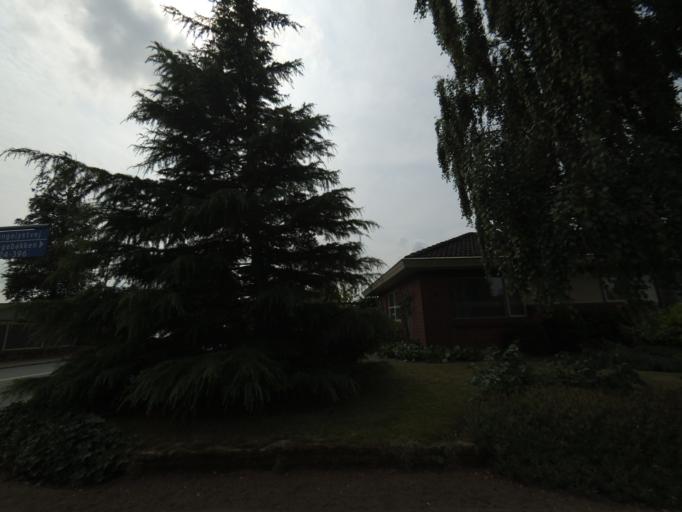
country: DK
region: South Denmark
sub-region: Odense Kommune
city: Bellinge
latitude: 55.3678
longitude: 10.3372
